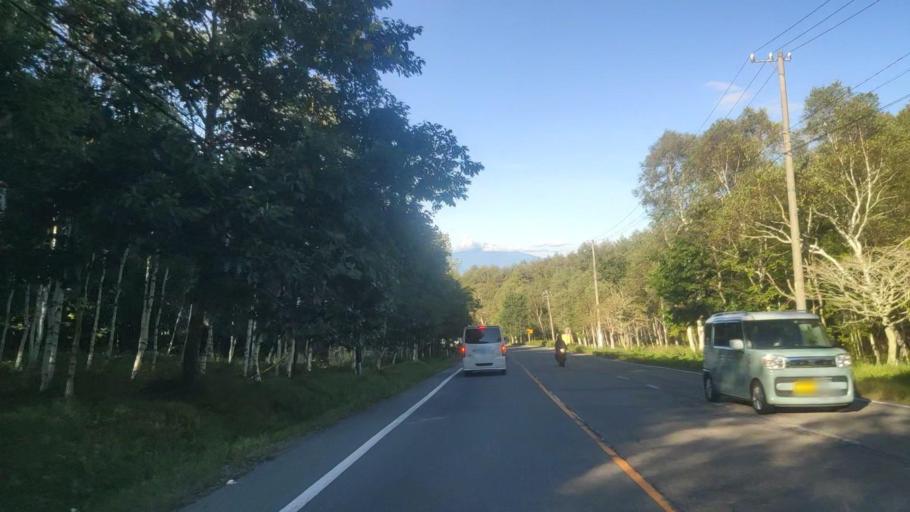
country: JP
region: Nagano
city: Kamimaruko
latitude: 36.1604
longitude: 138.2800
